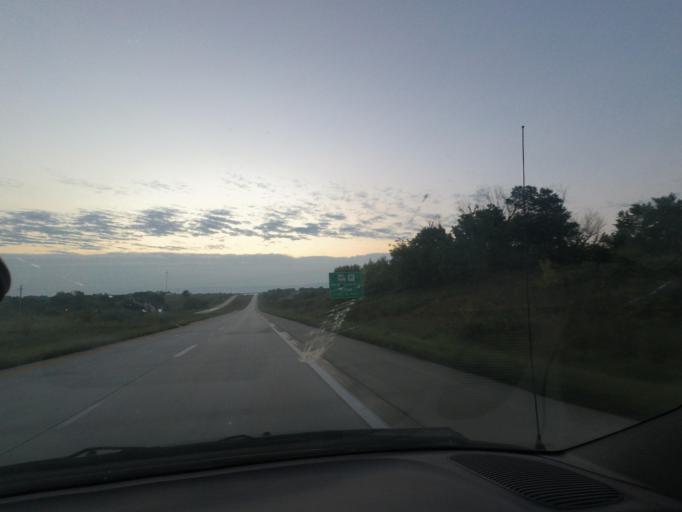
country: US
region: Missouri
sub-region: Linn County
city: Marceline
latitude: 39.7649
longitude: -92.7655
